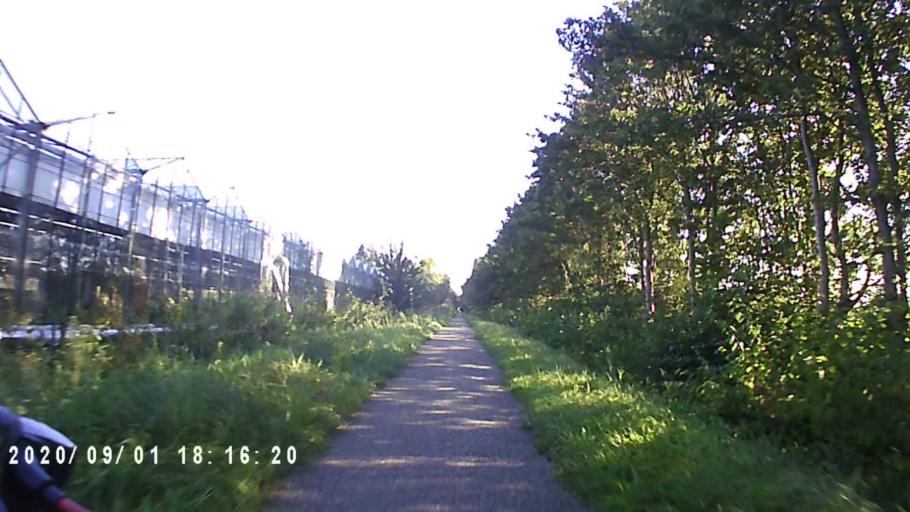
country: NL
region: Groningen
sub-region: Gemeente Hoogezand-Sappemeer
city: Sappemeer
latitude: 53.1767
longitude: 6.7862
